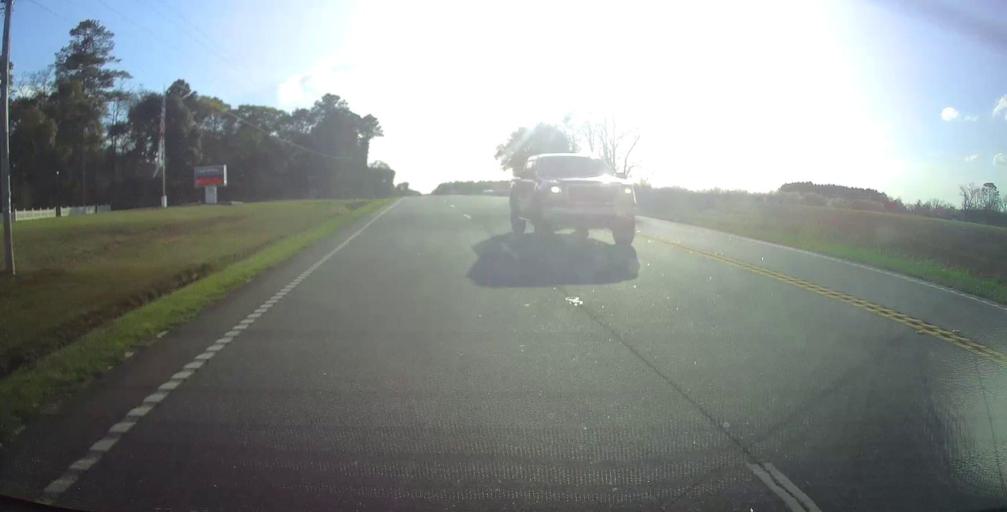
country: US
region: Georgia
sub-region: Tattnall County
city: Reidsville
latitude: 32.1075
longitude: -82.0899
